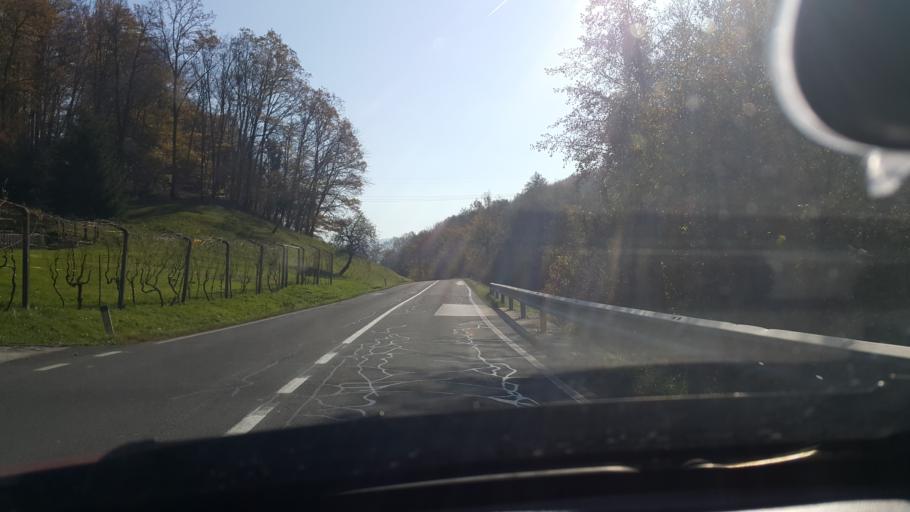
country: SI
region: Podcetrtek
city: Podcetrtek
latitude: 46.2122
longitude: 15.5850
